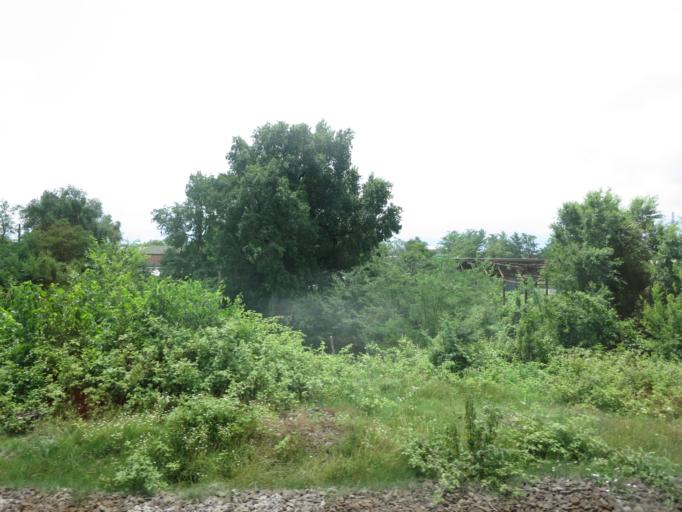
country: GE
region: Imereti
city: Kutaisi
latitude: 42.1981
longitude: 42.7221
